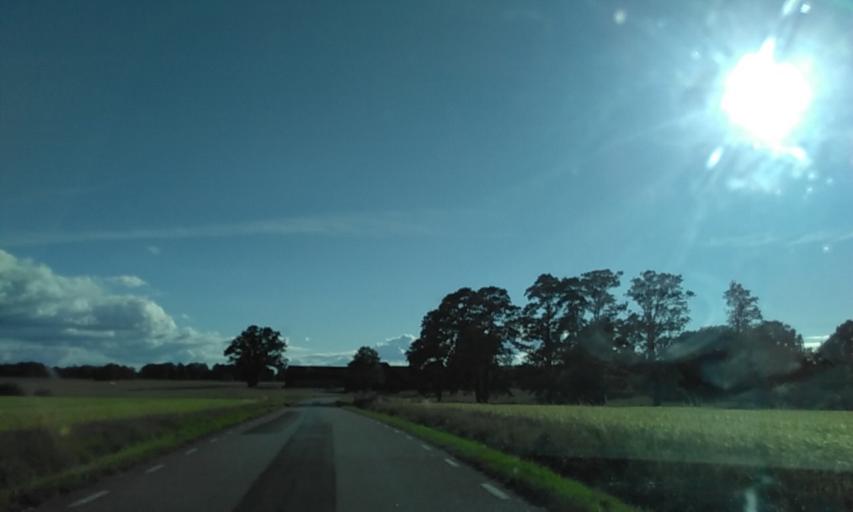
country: SE
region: Vaestra Goetaland
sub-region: Vara Kommun
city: Vara
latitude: 58.3715
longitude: 12.8801
